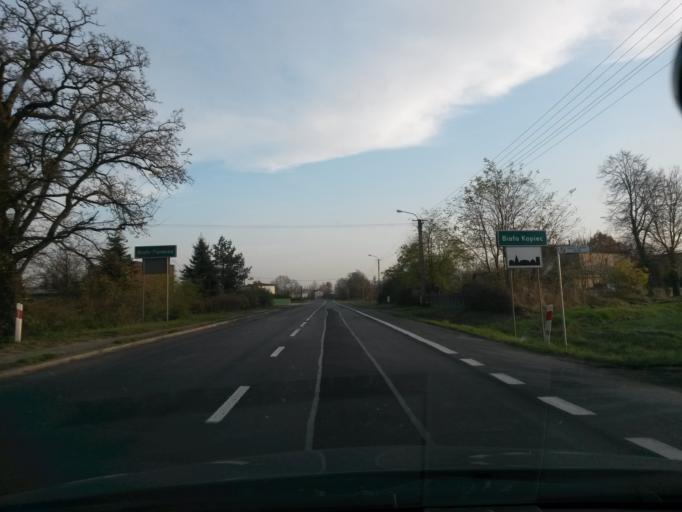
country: PL
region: Lodz Voivodeship
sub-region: Powiat wieruszowski
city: Walichnowy
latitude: 51.2717
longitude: 18.4338
